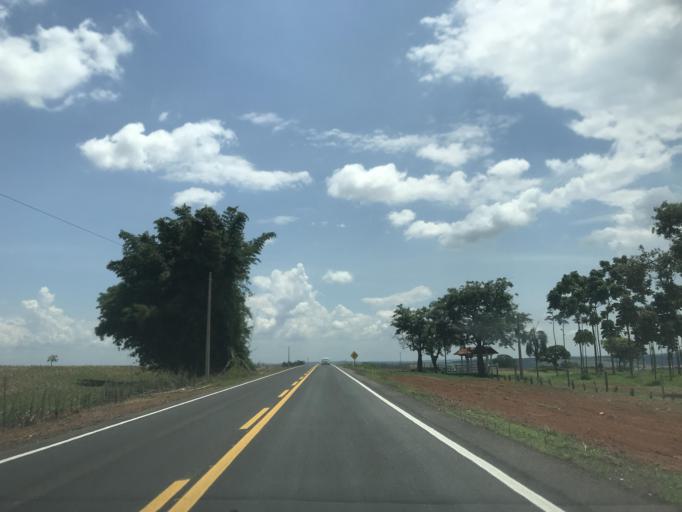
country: BR
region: Goias
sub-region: Bela Vista De Goias
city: Bela Vista de Goias
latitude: -17.0984
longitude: -48.6589
